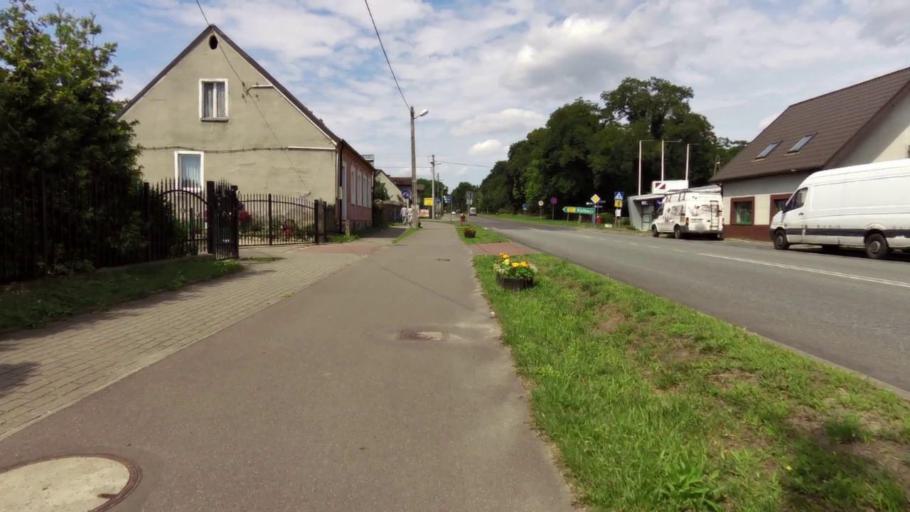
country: PL
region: West Pomeranian Voivodeship
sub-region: Powiat stargardzki
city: Kobylanka
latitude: 53.3450
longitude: 14.8699
